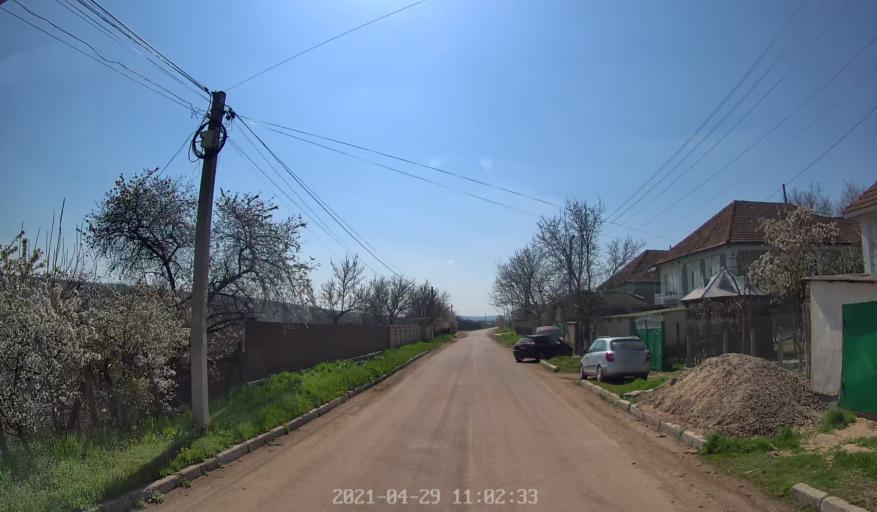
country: MD
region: Chisinau
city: Ciorescu
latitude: 47.1625
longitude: 28.9521
